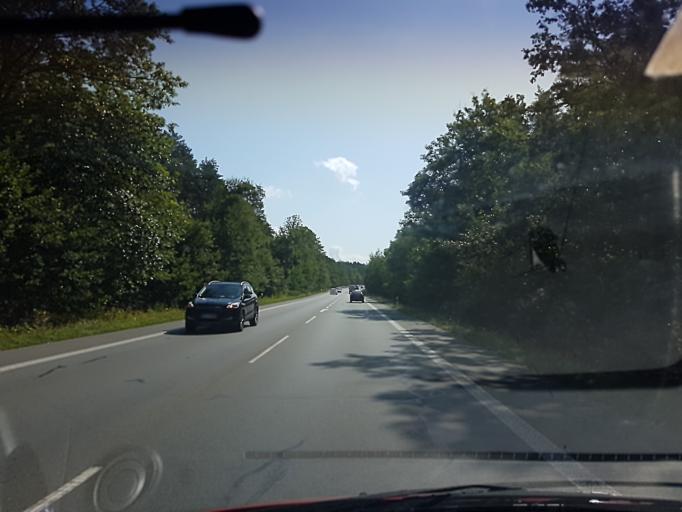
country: DE
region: Bavaria
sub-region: Regierungsbezirk Mittelfranken
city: Mohrendorf
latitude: 49.6156
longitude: 10.9634
